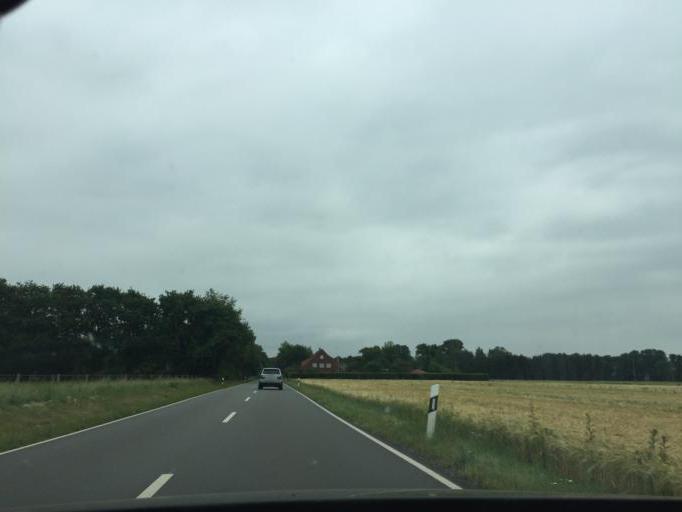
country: DE
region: North Rhine-Westphalia
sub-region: Regierungsbezirk Munster
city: Lienen
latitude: 52.1125
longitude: 7.9099
